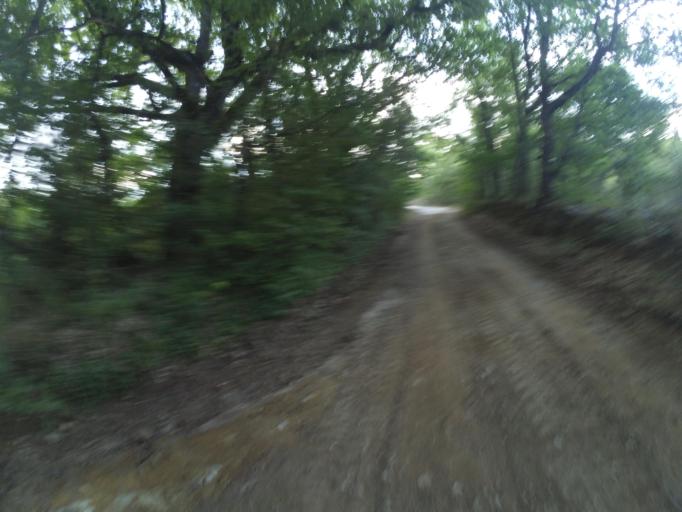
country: IT
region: Tuscany
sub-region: Province of Arezzo
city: Castiglion Fibocchi
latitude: 43.5415
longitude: 11.7679
